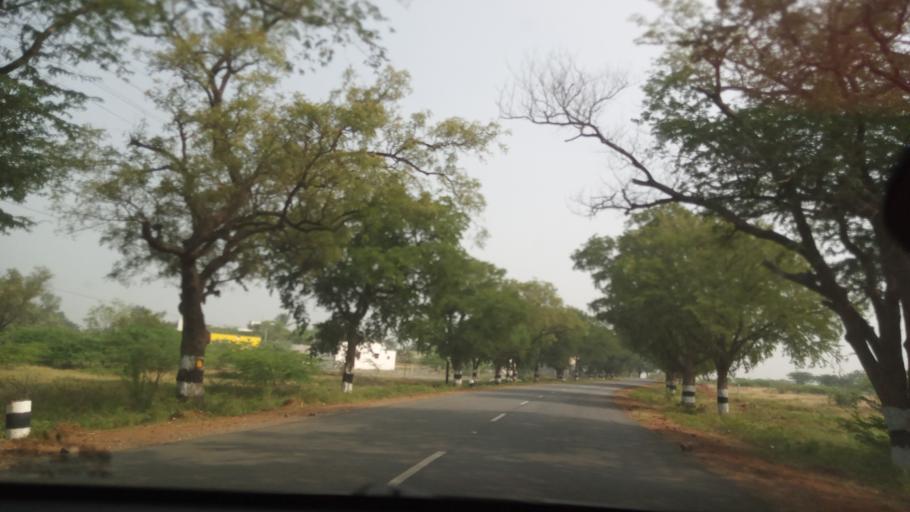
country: IN
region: Tamil Nadu
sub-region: Erode
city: Punjai Puliyampatti
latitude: 11.4259
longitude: 77.1957
